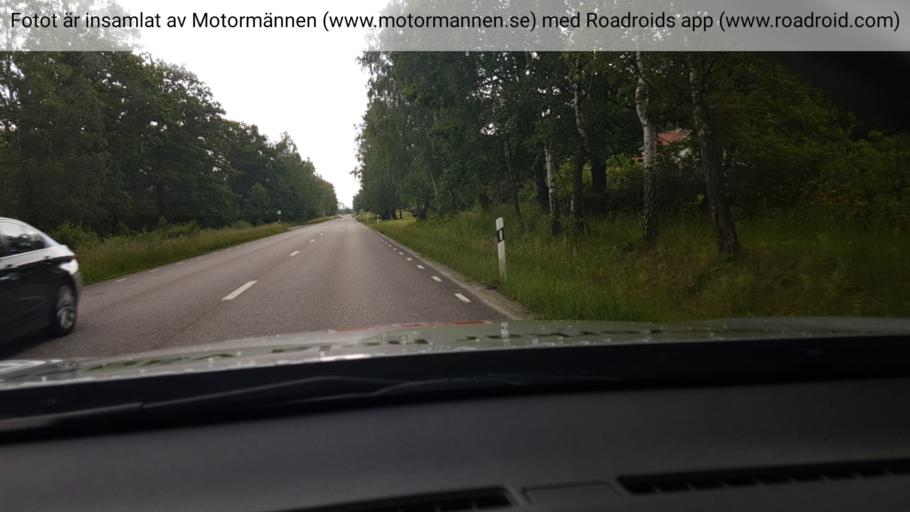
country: SE
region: Vaestra Goetaland
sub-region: Hjo Kommun
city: Hjo
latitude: 58.1574
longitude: 14.2118
